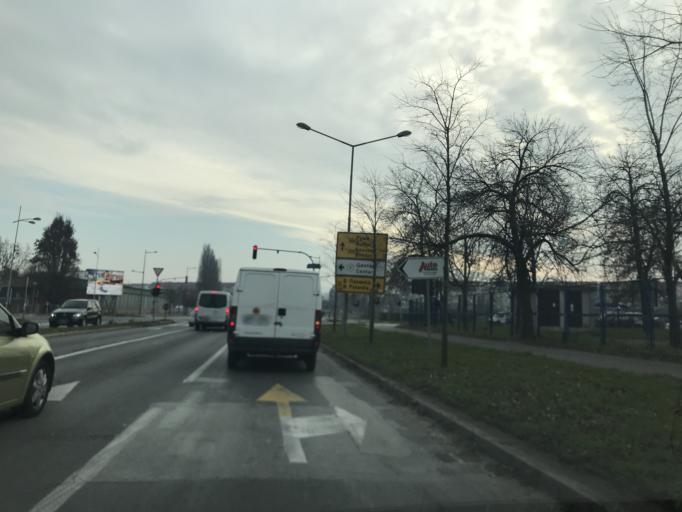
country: RS
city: Veternik
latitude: 45.2452
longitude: 19.7944
